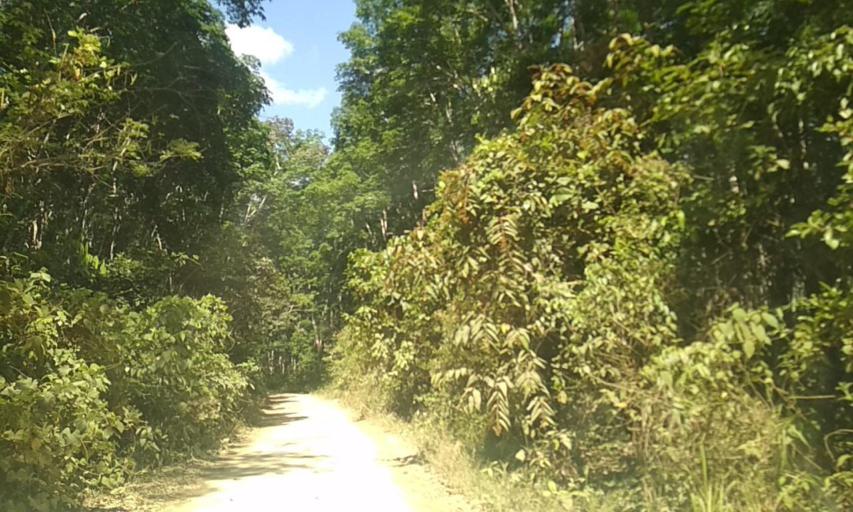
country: MX
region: Veracruz
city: Las Choapas
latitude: 17.7930
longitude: -94.1461
